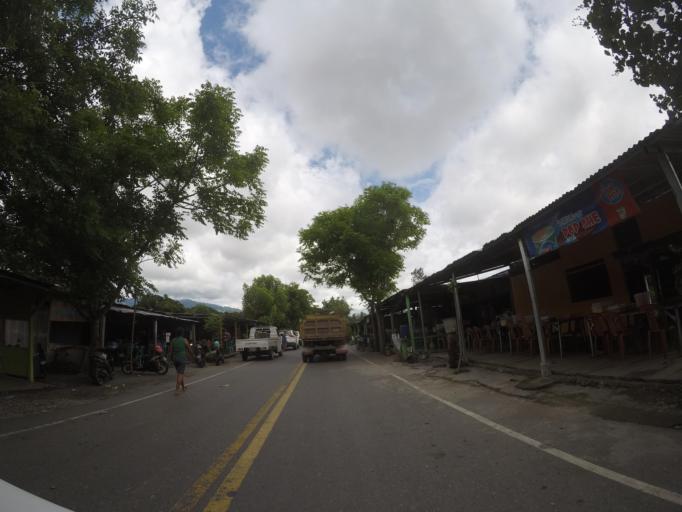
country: TL
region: Liquica
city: Maubara
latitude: -8.7389
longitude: 125.1349
